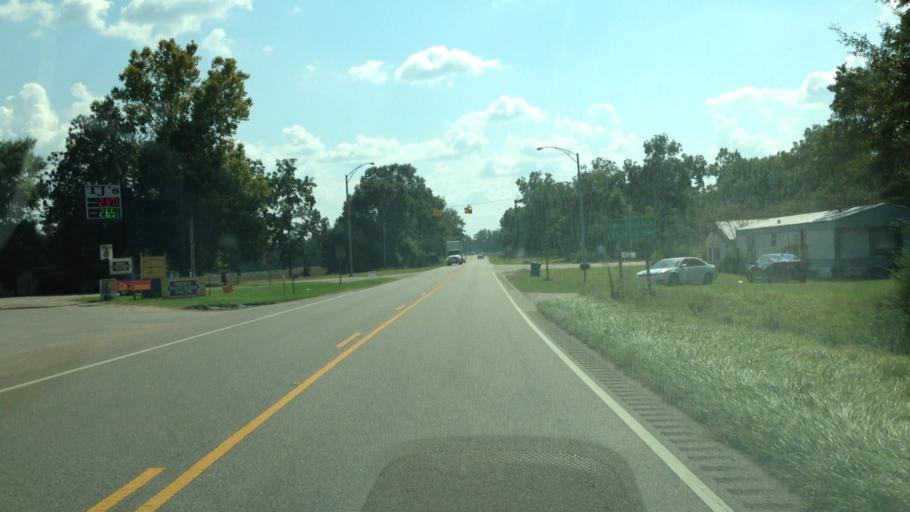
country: US
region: Florida
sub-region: Okaloosa County
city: Crestview
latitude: 31.0228
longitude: -86.6124
